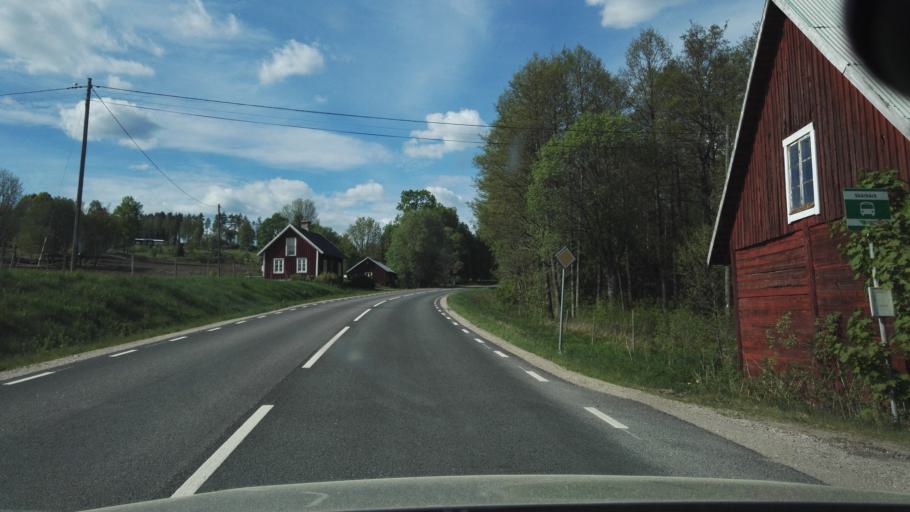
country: SE
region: Kronoberg
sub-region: Vaxjo Kommun
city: Braas
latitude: 57.1532
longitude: 14.9634
